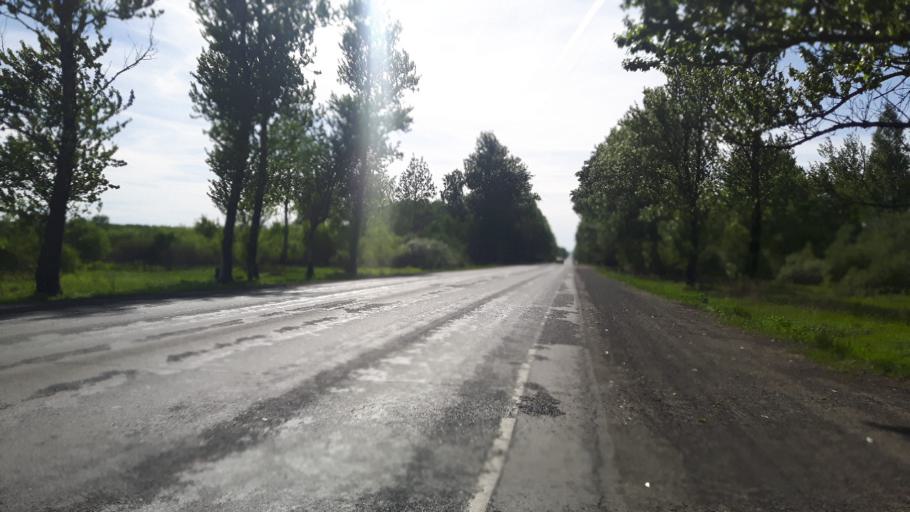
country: RU
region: Leningrad
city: Ivangorod
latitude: 59.3814
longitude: 28.3418
